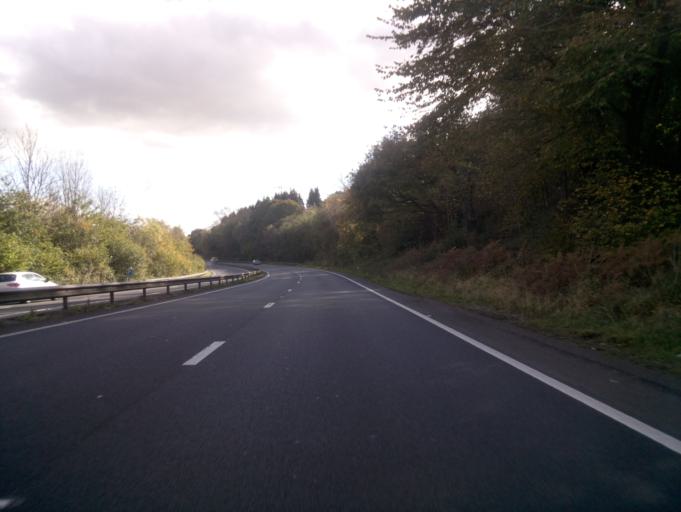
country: GB
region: Wales
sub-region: Merthyr Tydfil County Borough
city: Treharris
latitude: 51.6788
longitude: -3.3394
